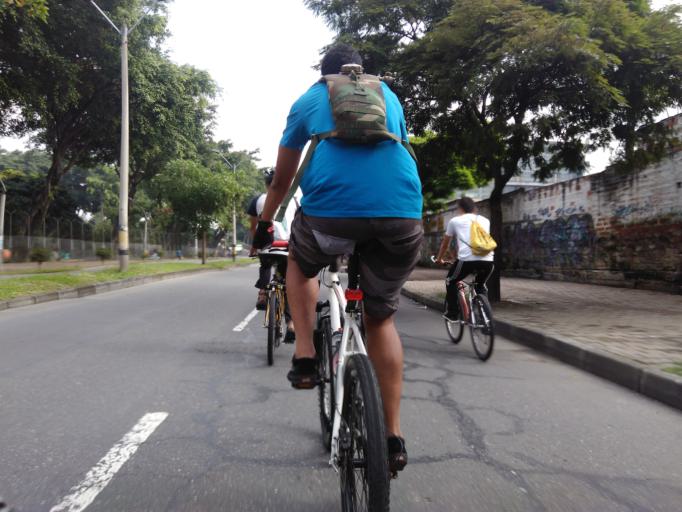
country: CO
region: Antioquia
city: Medellin
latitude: 6.2661
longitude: -75.5670
